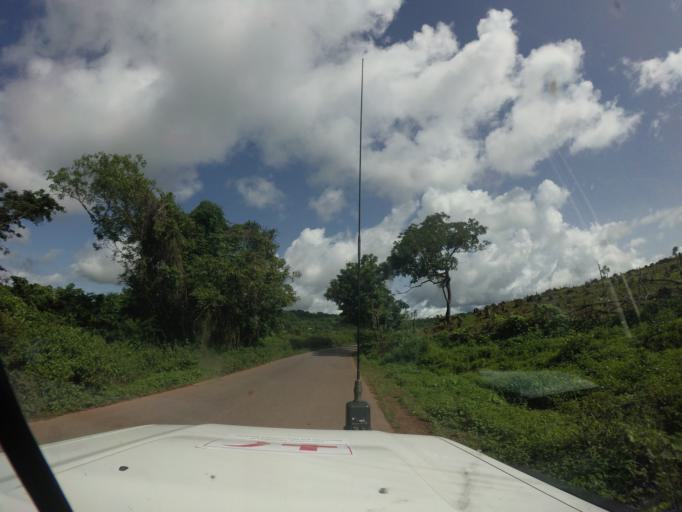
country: GN
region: Mamou
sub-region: Mamou Prefecture
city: Mamou
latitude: 10.3065
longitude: -12.2770
